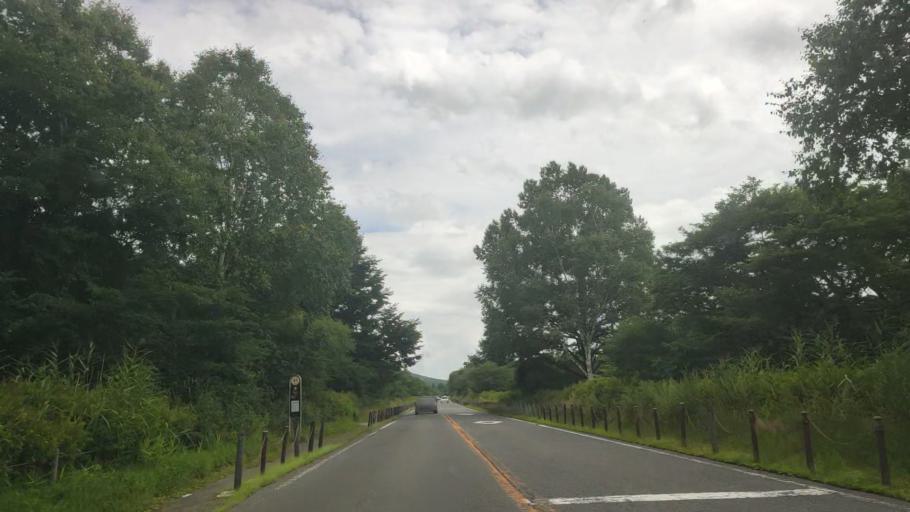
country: JP
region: Tochigi
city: Nikko
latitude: 36.7857
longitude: 139.4444
